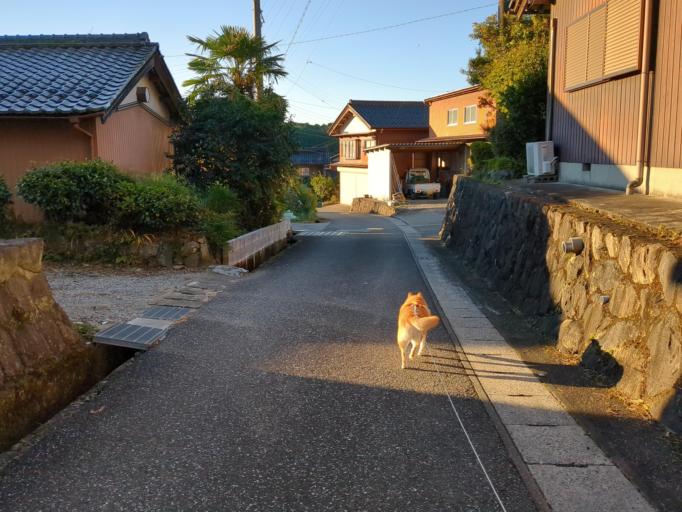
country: JP
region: Gifu
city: Tarui
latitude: 35.4029
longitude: 136.5279
